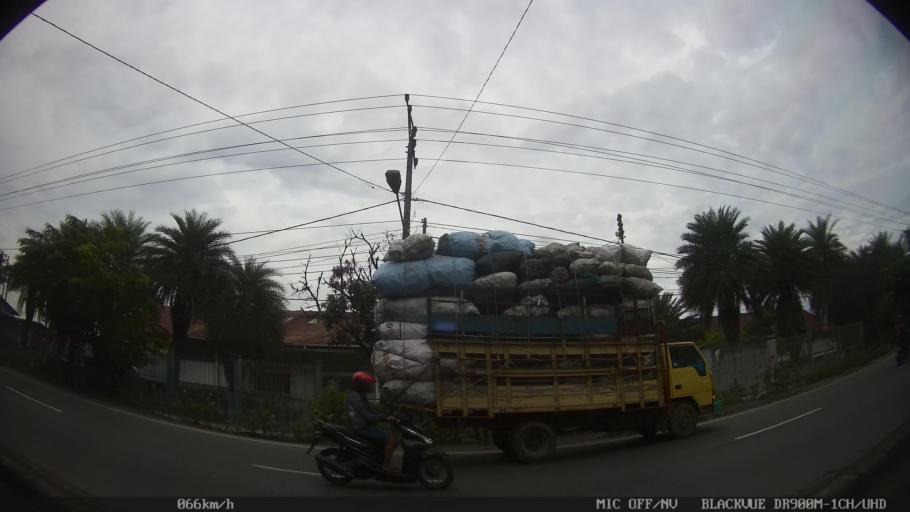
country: ID
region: North Sumatra
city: Sunggal
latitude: 3.5996
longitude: 98.5697
